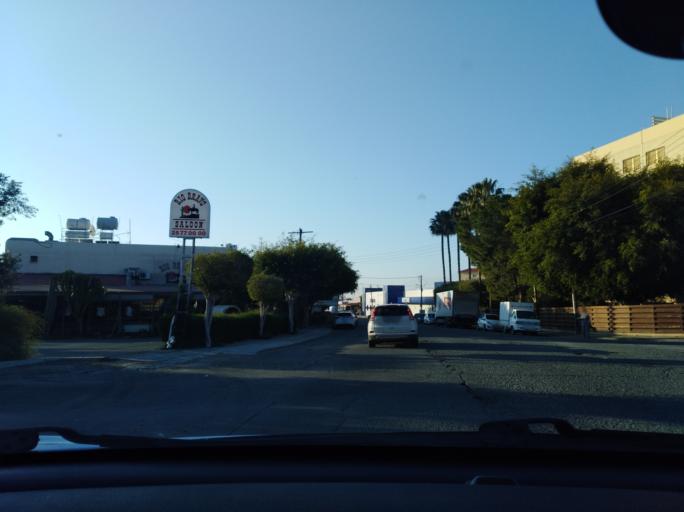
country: CY
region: Limassol
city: Mouttagiaka
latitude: 34.7045
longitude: 33.1064
